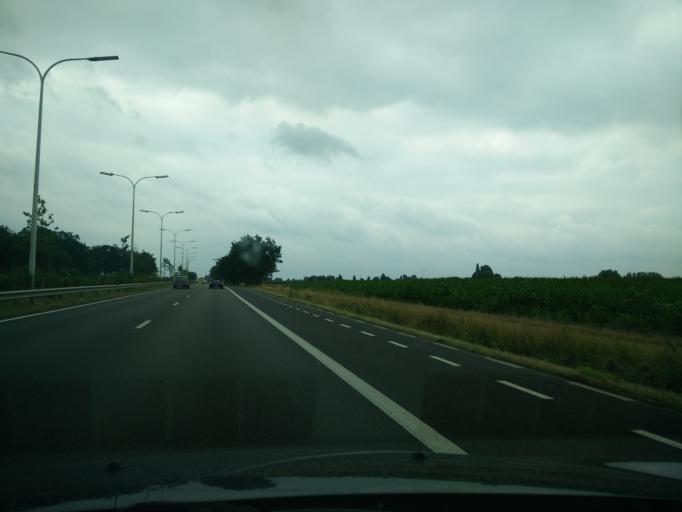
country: BE
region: Flanders
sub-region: Provincie Oost-Vlaanderen
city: Zingem
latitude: 50.8968
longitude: 3.6162
